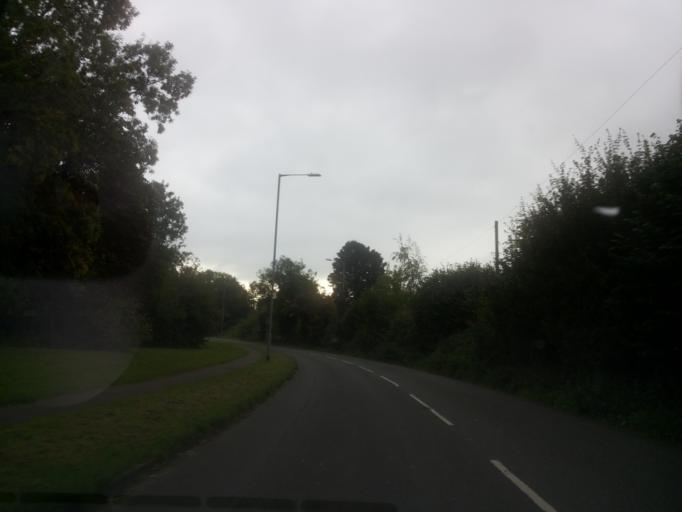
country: GB
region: England
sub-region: Buckinghamshire
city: Wendover
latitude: 51.7585
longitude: -0.7424
